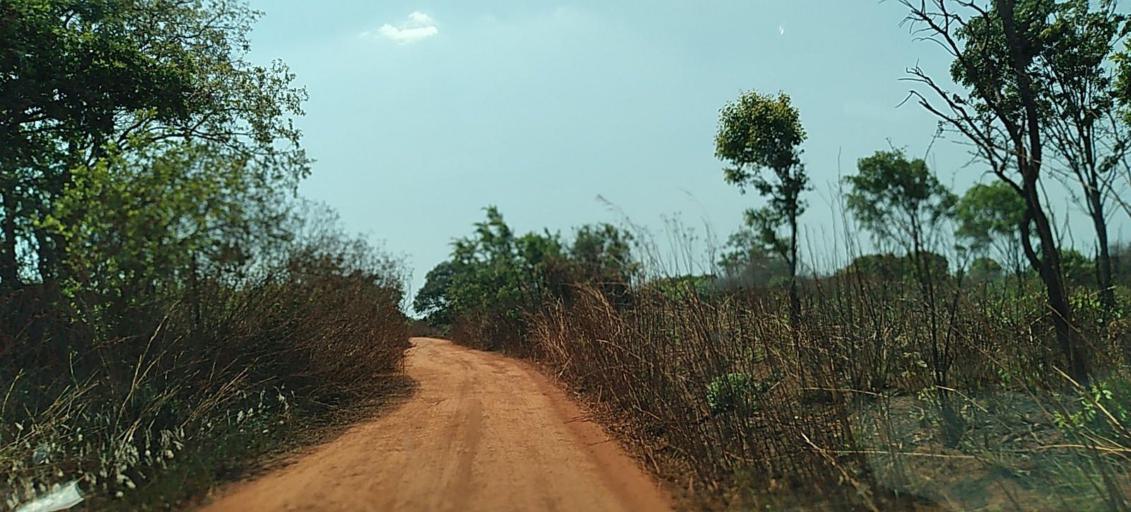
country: ZM
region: North-Western
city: Solwezi
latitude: -12.1331
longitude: 26.3163
